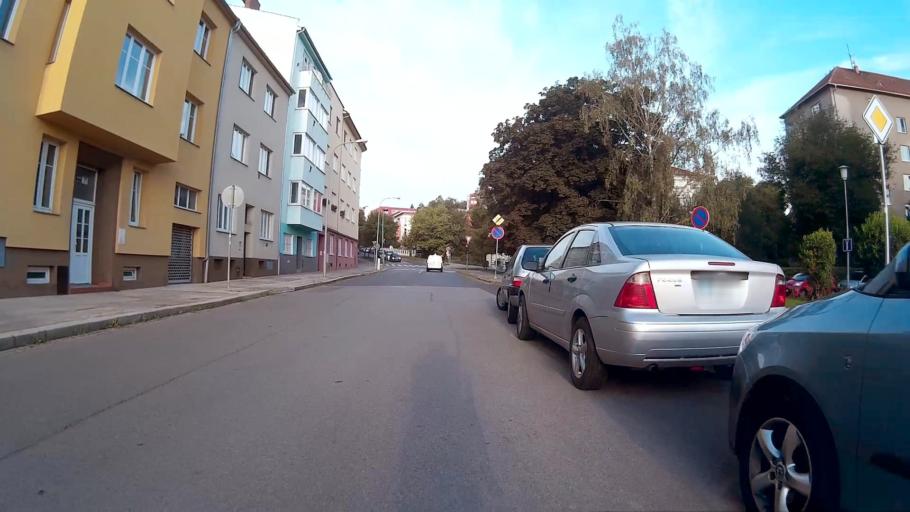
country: CZ
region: South Moravian
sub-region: Mesto Brno
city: Brno
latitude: 49.1828
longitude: 16.5960
